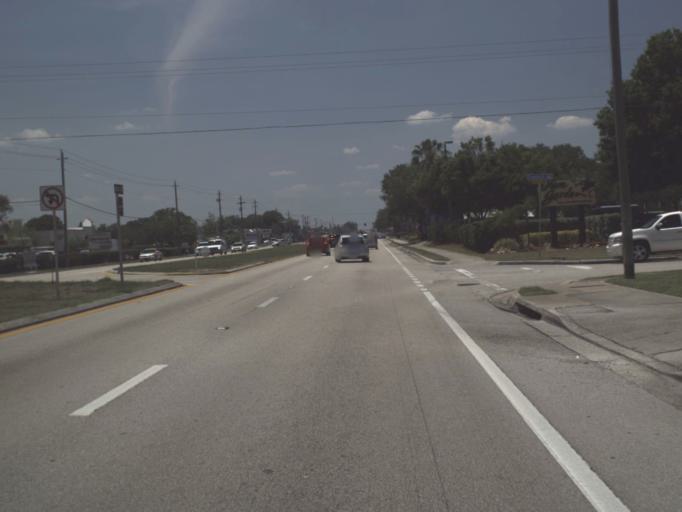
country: US
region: Florida
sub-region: Brevard County
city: West Melbourne
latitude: 28.0790
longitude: -80.6617
